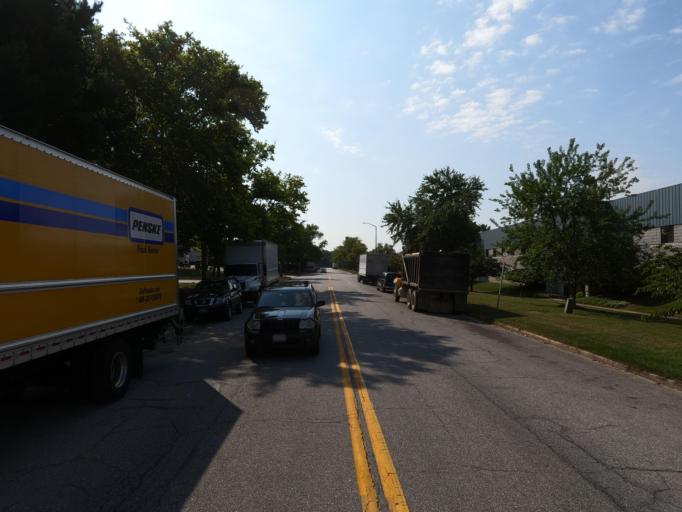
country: US
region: Maryland
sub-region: Howard County
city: Savage
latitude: 39.1725
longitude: -76.8418
